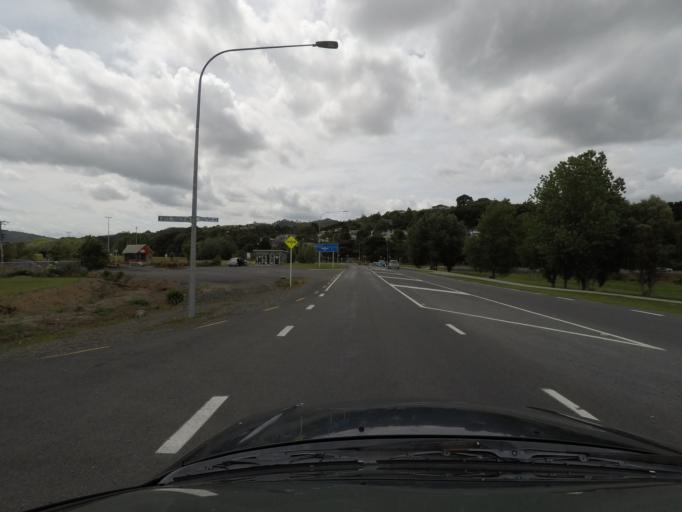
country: NZ
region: Northland
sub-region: Whangarei
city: Whangarei
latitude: -35.7327
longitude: 174.3429
